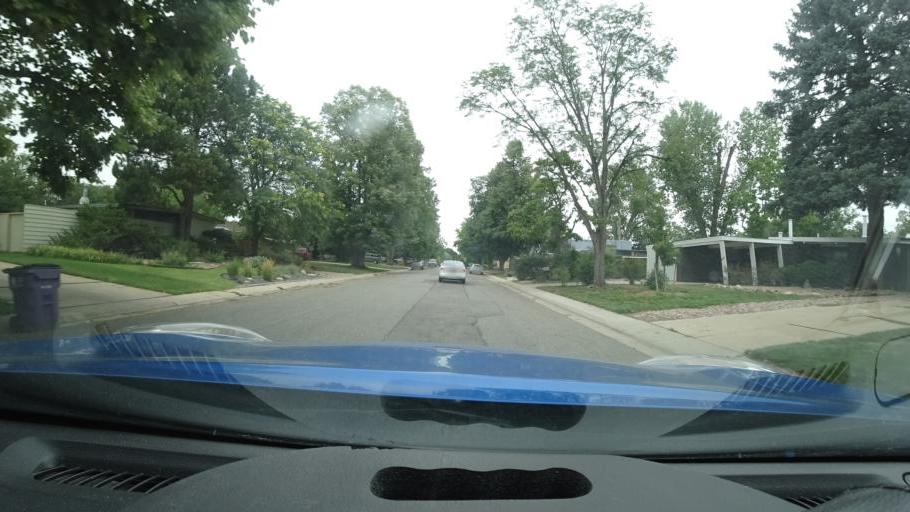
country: US
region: Colorado
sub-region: Arapahoe County
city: Glendale
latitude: 39.6846
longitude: -104.9183
